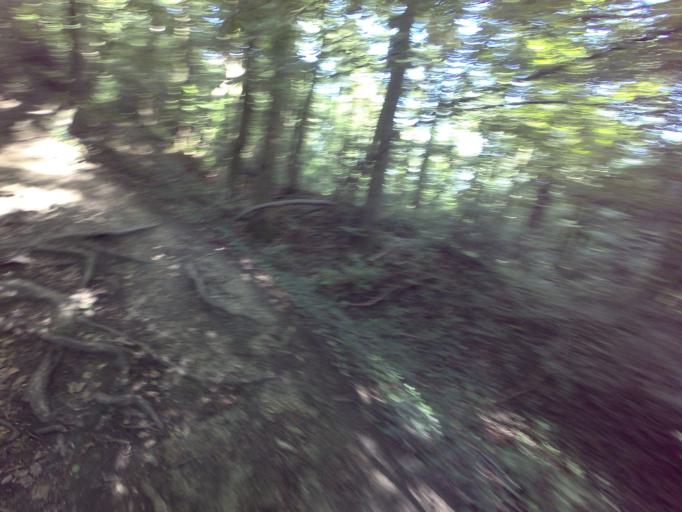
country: NL
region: Limburg
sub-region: Gemeente Vaals
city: Vaals
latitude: 50.7542
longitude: 6.0059
